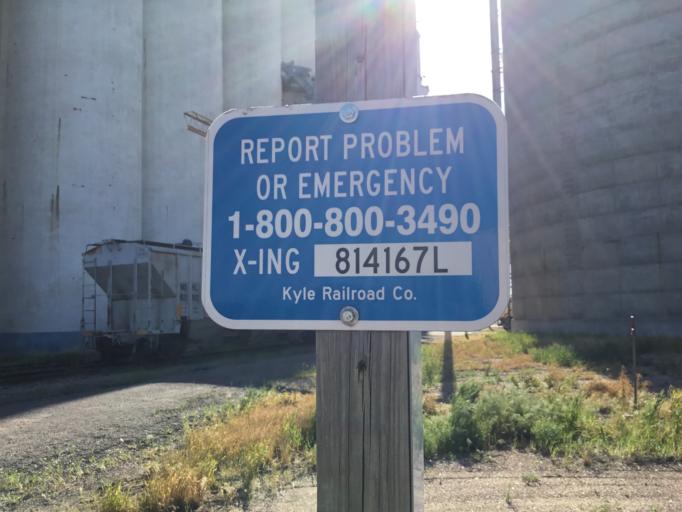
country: US
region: Kansas
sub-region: Mitchell County
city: Beloit
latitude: 39.4565
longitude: -98.1071
